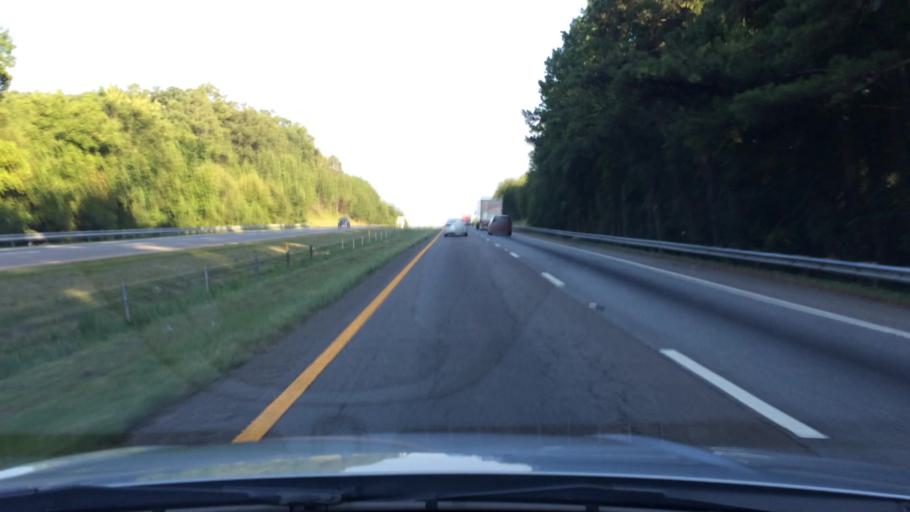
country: US
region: South Carolina
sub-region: Newberry County
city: Prosperity
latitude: 34.2648
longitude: -81.5045
